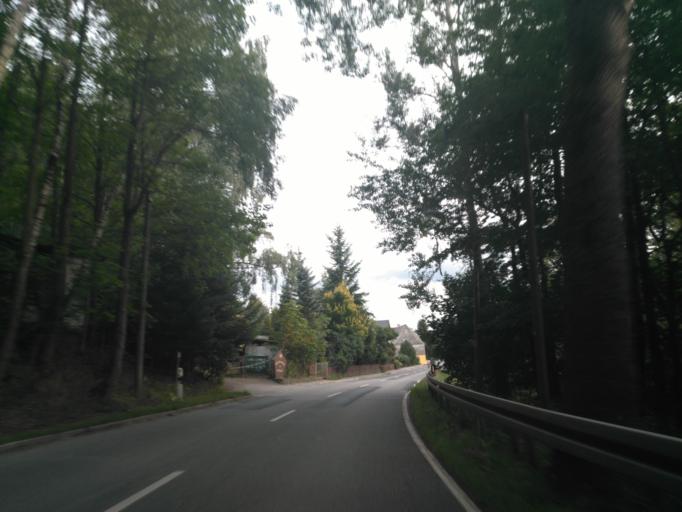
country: DE
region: Saxony
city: Tannenberg
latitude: 50.5924
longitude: 12.9485
